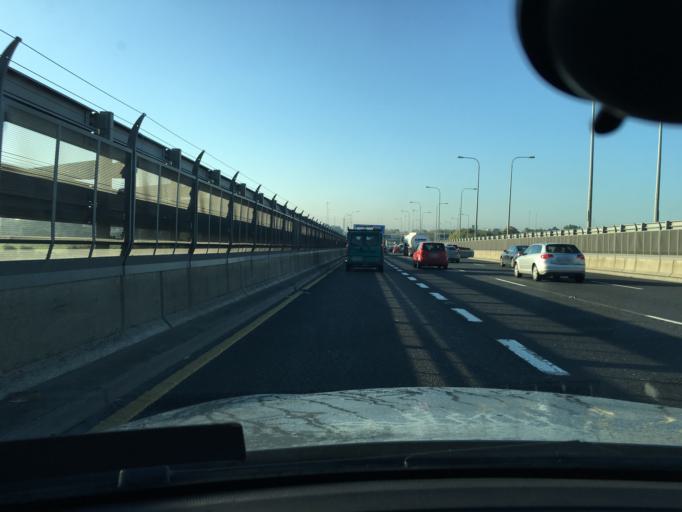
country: IE
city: Palmerstown
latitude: 53.3618
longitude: -6.3826
